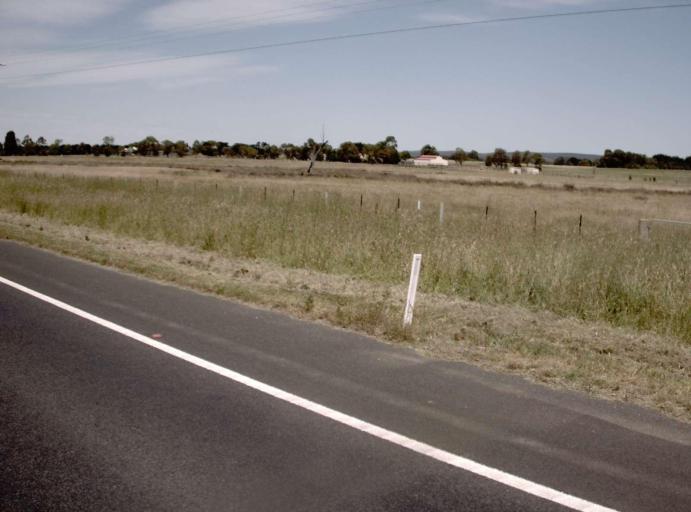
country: AU
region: Victoria
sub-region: Wellington
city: Heyfield
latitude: -38.1574
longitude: 146.7474
